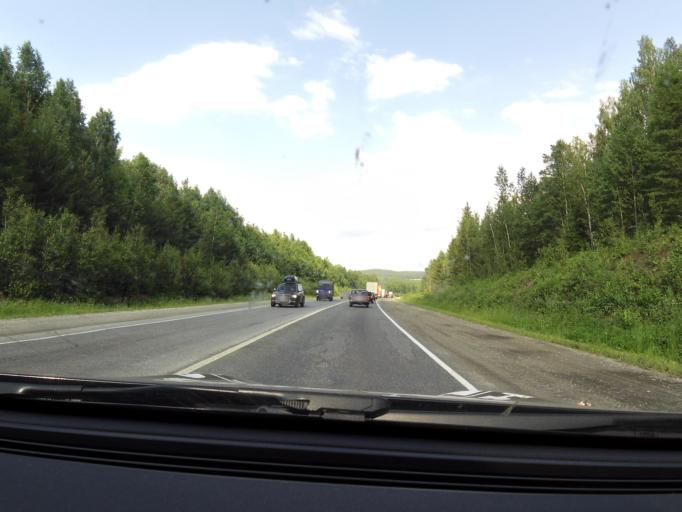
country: RU
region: Sverdlovsk
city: Talitsa
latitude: 56.8415
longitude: 60.0083
